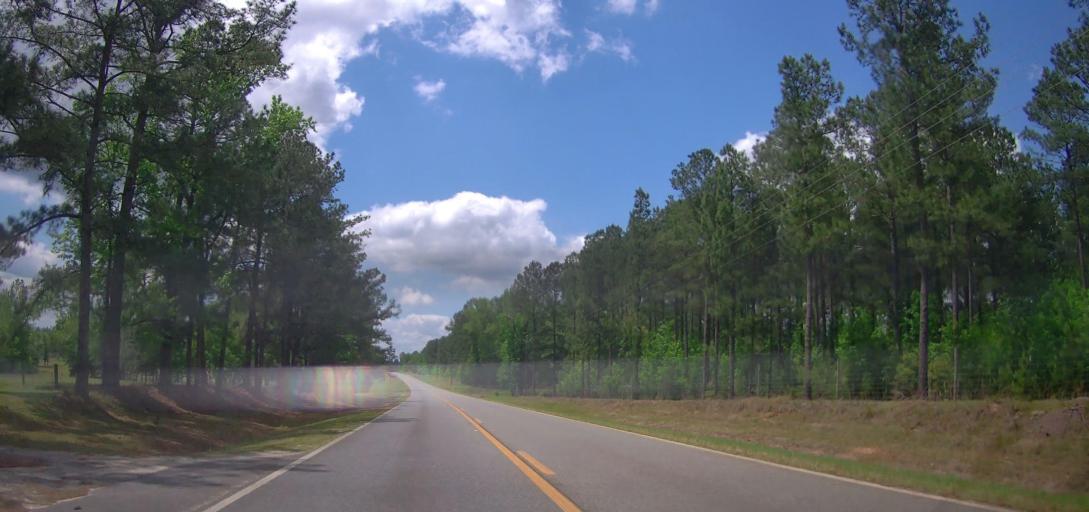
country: US
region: Georgia
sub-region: Laurens County
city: East Dublin
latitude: 32.5252
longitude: -82.7424
